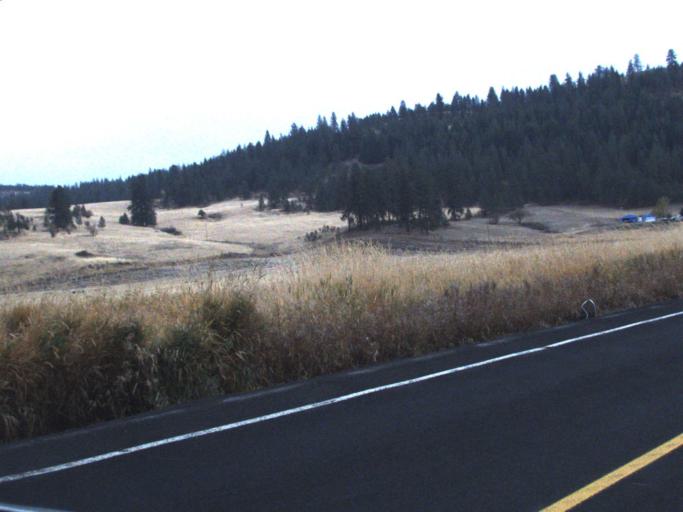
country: US
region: Washington
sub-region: Lincoln County
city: Davenport
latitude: 47.8858
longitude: -118.2642
